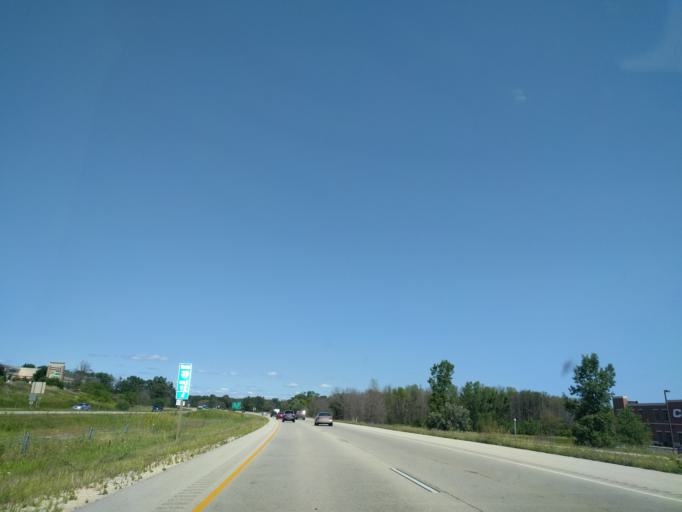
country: US
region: Wisconsin
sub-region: Ozaukee County
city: Grafton
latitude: 43.3221
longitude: -87.9192
